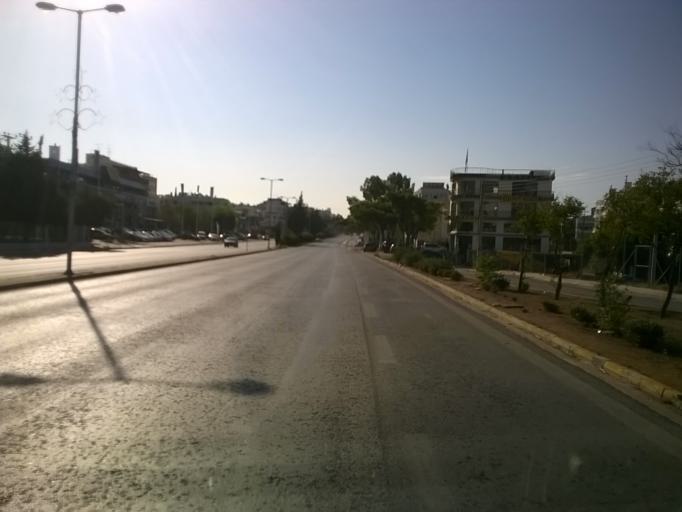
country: GR
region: Attica
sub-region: Nomarchia Athinas
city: Glyfada
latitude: 37.8606
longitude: 23.7632
